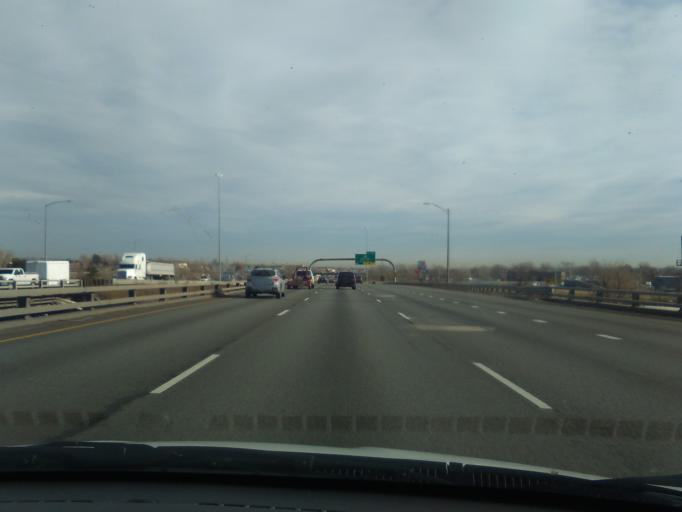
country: US
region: Colorado
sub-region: Jefferson County
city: Applewood
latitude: 39.7796
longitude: -105.1383
